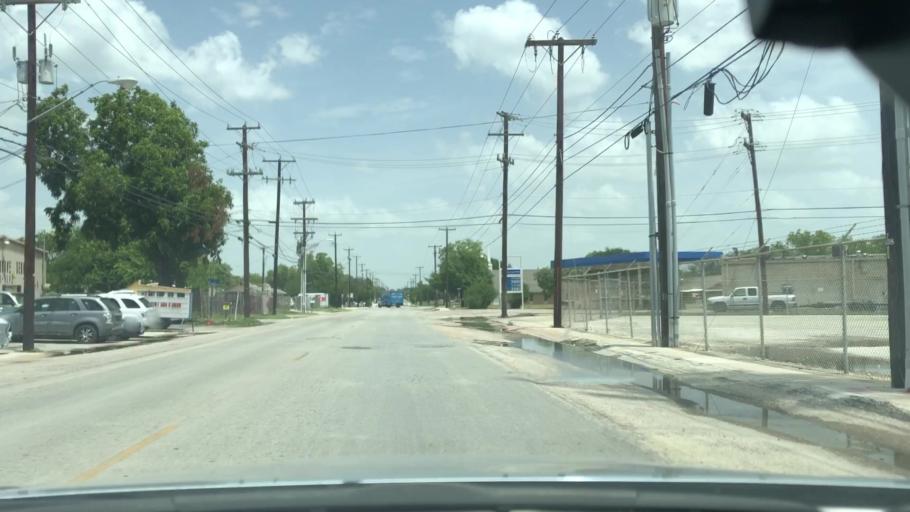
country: US
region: Texas
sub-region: Bexar County
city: Kirby
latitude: 29.4659
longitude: -98.3925
